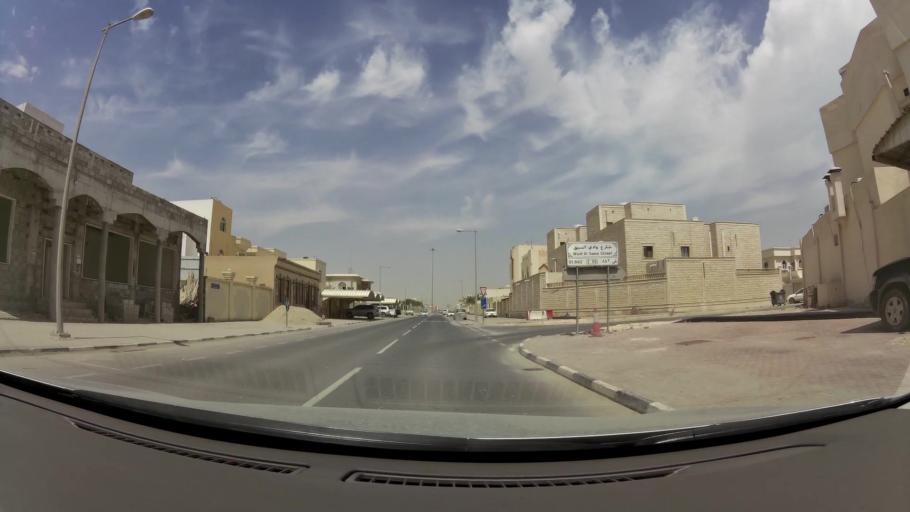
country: QA
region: Baladiyat ar Rayyan
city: Ar Rayyan
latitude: 25.2587
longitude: 51.4263
